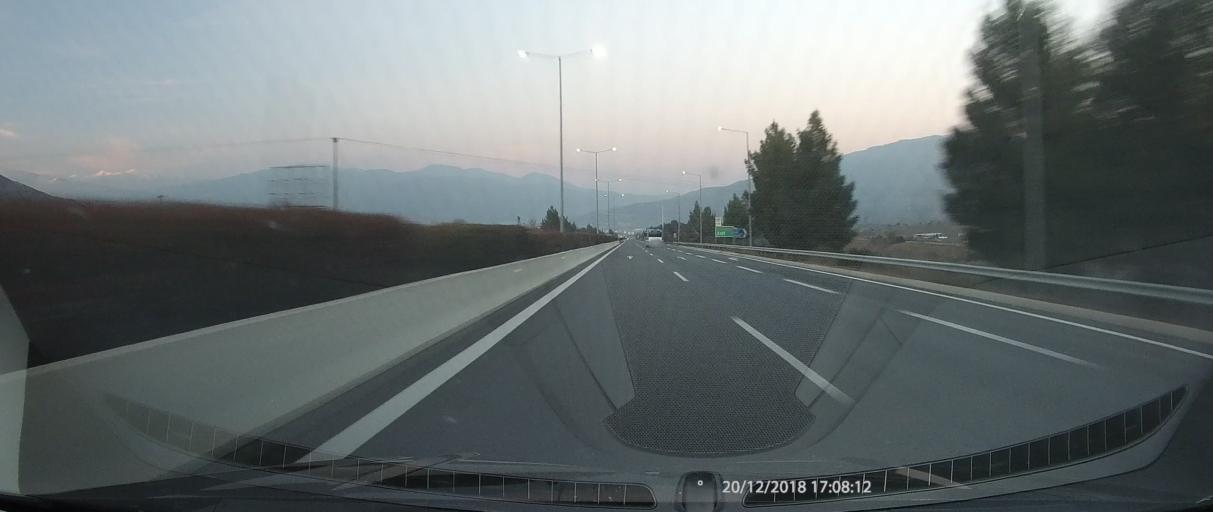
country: GR
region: Thessaly
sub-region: Nomos Larisis
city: Makrychori
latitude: 39.7935
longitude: 22.4966
